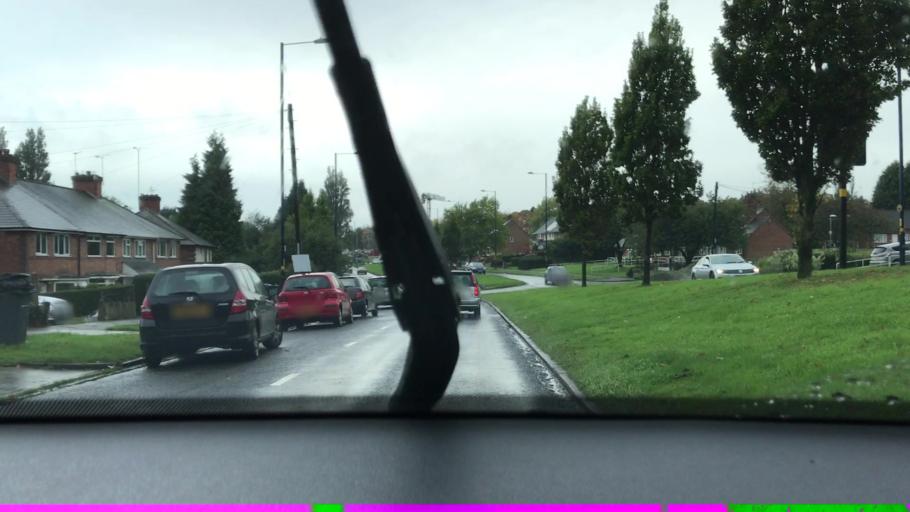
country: GB
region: England
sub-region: City and Borough of Birmingham
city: Bartley Green
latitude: 52.4607
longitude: -1.9789
